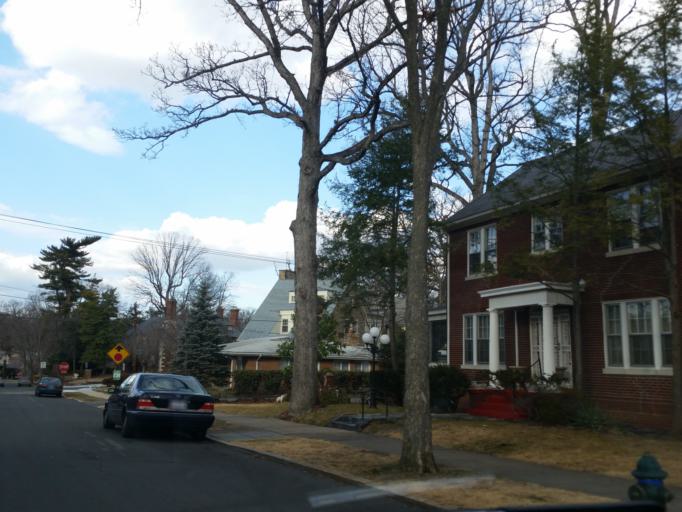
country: US
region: Maryland
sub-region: Montgomery County
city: Takoma Park
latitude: 38.9462
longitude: -77.0388
